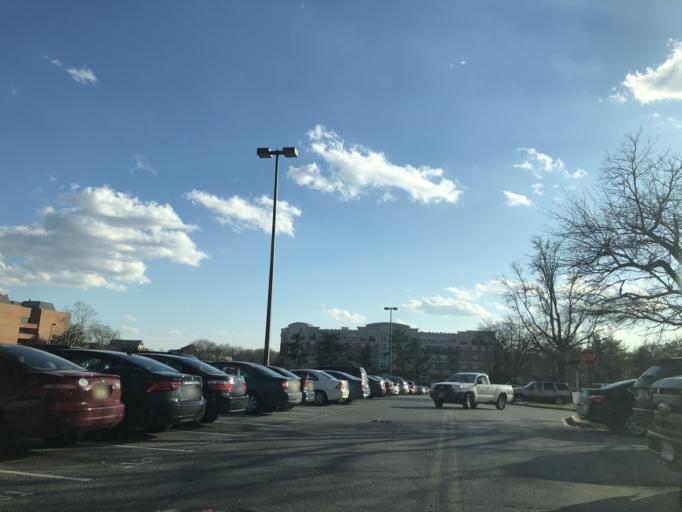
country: US
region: Maryland
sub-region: Prince George's County
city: College Park
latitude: 38.9866
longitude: -76.9496
